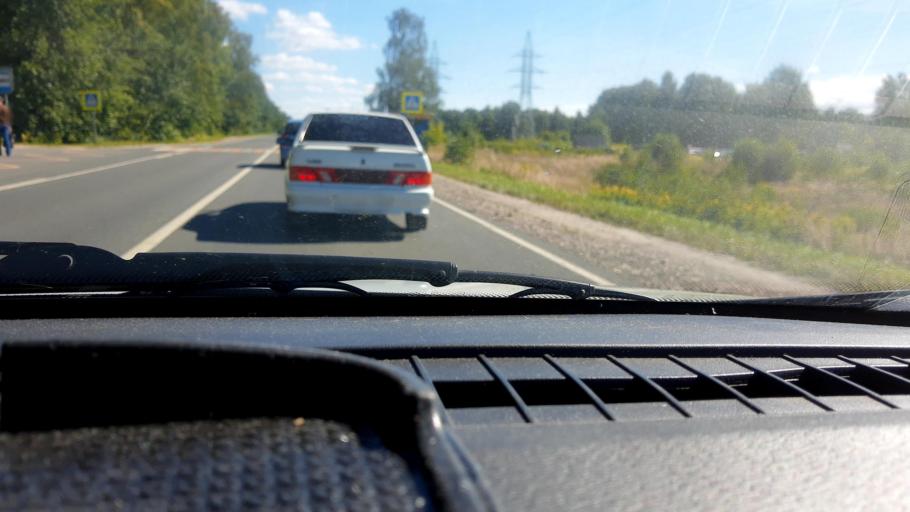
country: RU
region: Nizjnij Novgorod
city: Lukino
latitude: 56.4579
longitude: 43.6248
